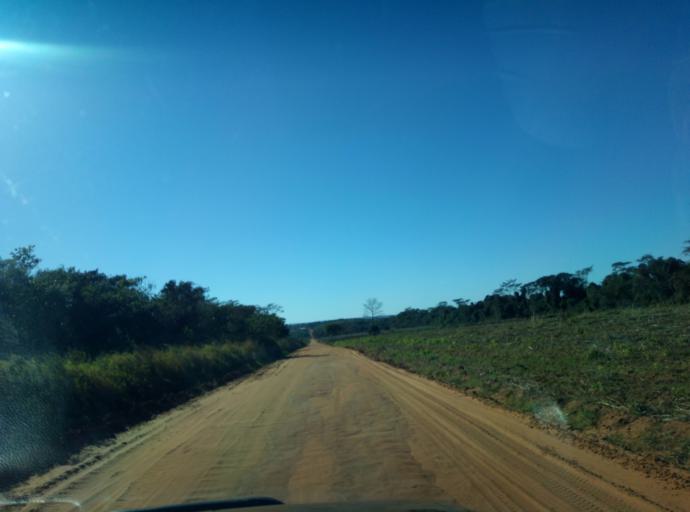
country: PY
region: Caaguazu
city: Doctor Cecilio Baez
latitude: -25.1620
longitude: -56.2703
